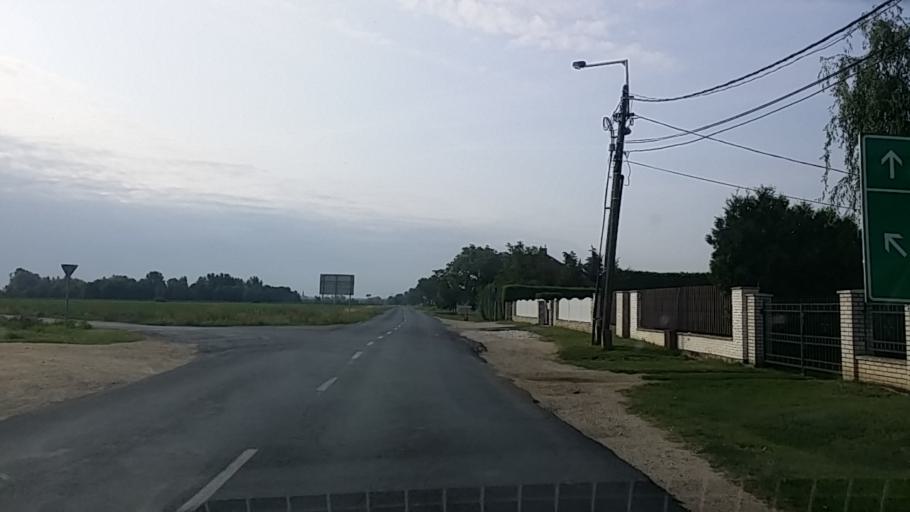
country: HU
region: Gyor-Moson-Sopron
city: Fertod
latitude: 47.6150
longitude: 16.8887
